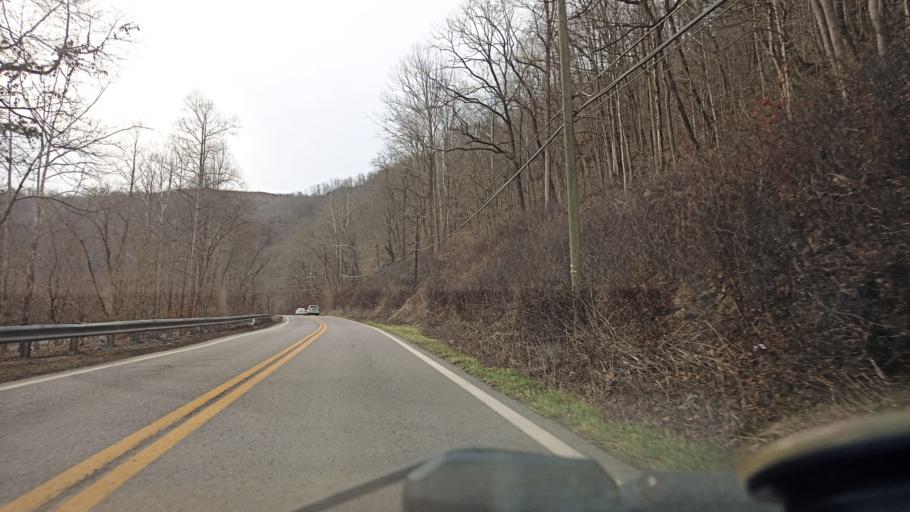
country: US
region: West Virginia
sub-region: Mingo County
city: Gilbert Creek
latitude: 37.6437
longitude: -81.8700
